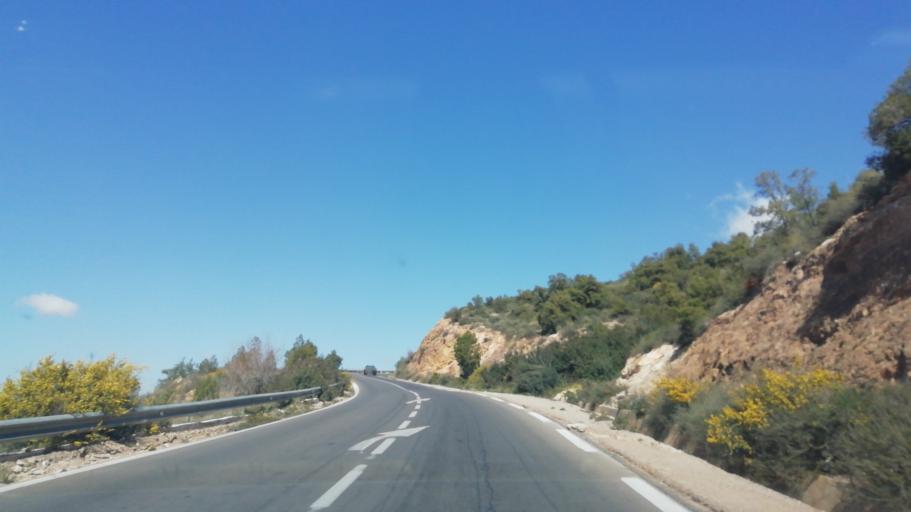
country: DZ
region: Mascara
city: Mascara
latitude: 35.4878
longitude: 0.1471
